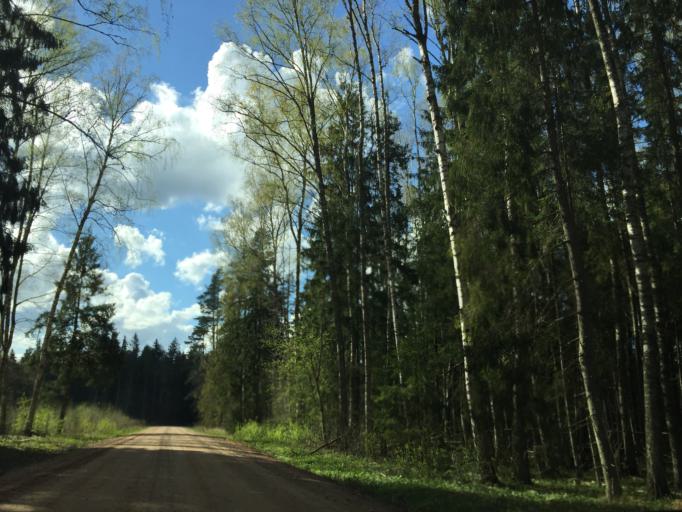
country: LV
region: Beverina
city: Murmuiza
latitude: 57.4713
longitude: 25.5338
